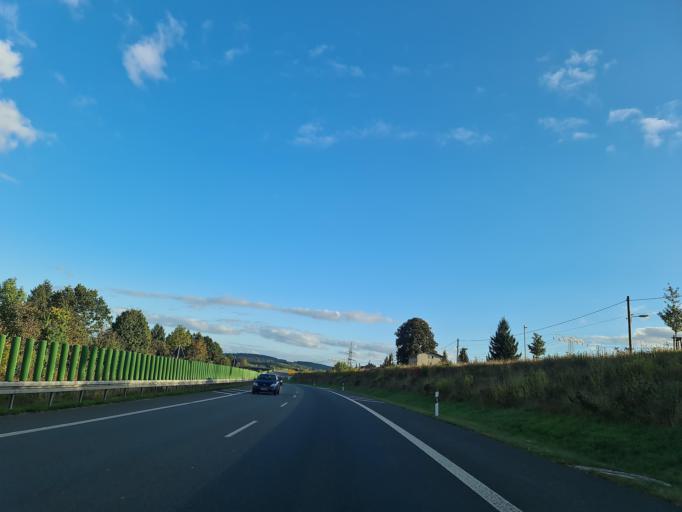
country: DE
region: Thuringia
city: Crimla
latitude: 50.8296
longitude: 12.0724
